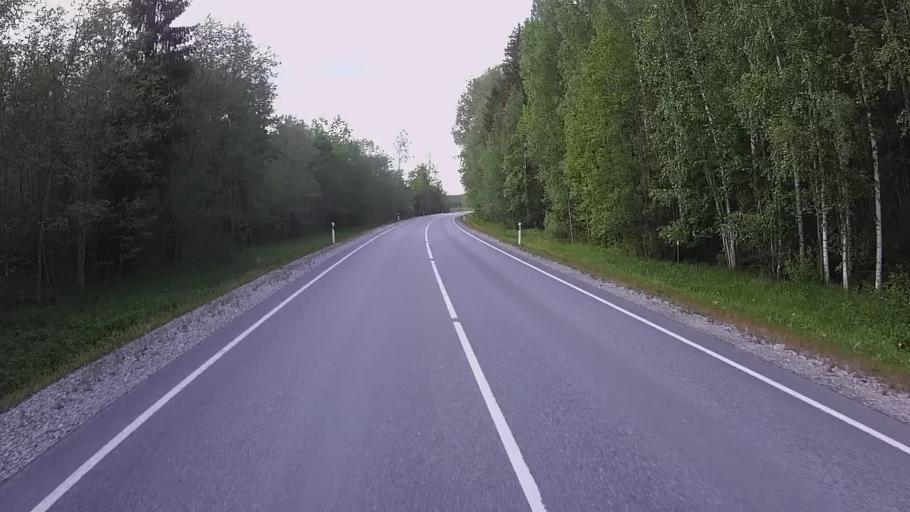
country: EE
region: Jogevamaa
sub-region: Mustvee linn
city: Mustvee
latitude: 58.8723
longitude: 26.8229
